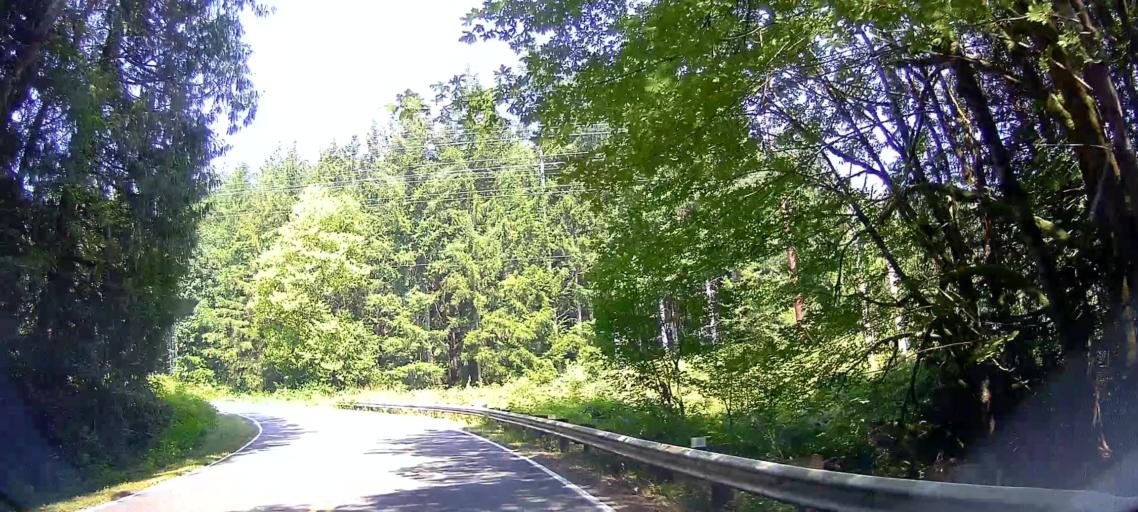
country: US
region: Washington
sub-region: Snohomish County
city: Bryant
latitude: 48.2688
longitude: -122.1671
